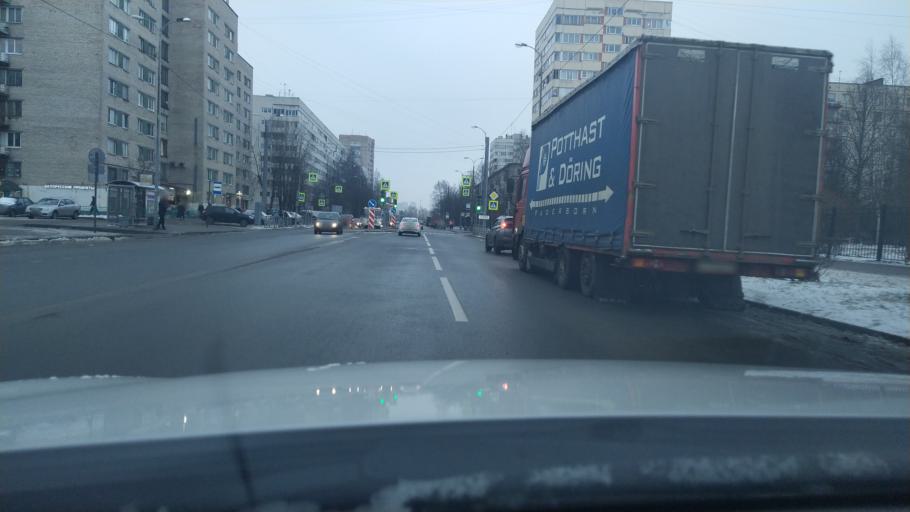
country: RU
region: St.-Petersburg
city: Grazhdanka
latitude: 60.0462
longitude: 30.3896
